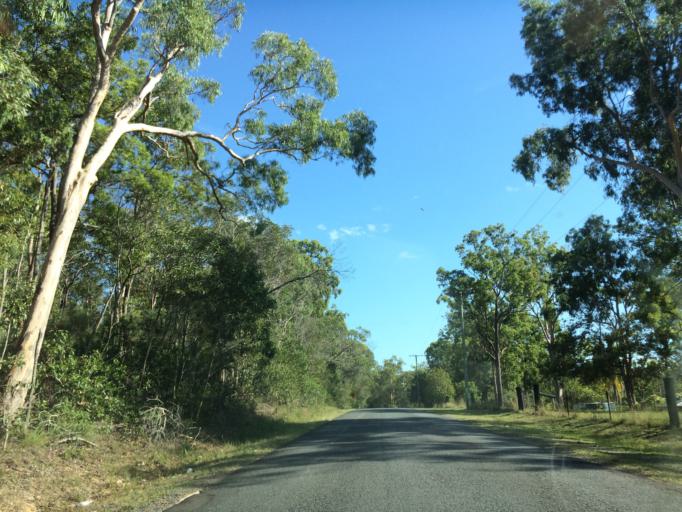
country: AU
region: Queensland
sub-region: Ipswich
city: Springfield Lakes
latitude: -27.7060
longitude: 152.9567
